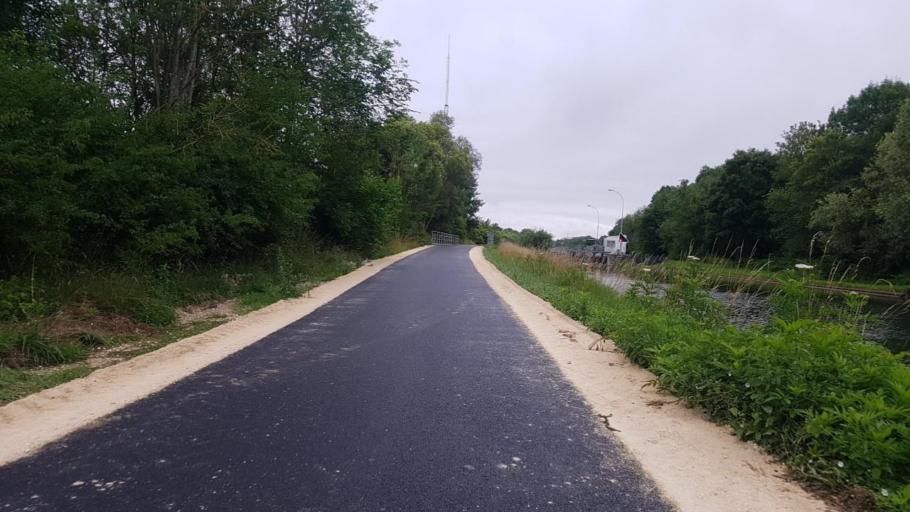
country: FR
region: Champagne-Ardenne
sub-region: Departement de la Marne
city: Vitry-le-Francois
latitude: 48.8077
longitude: 4.5216
